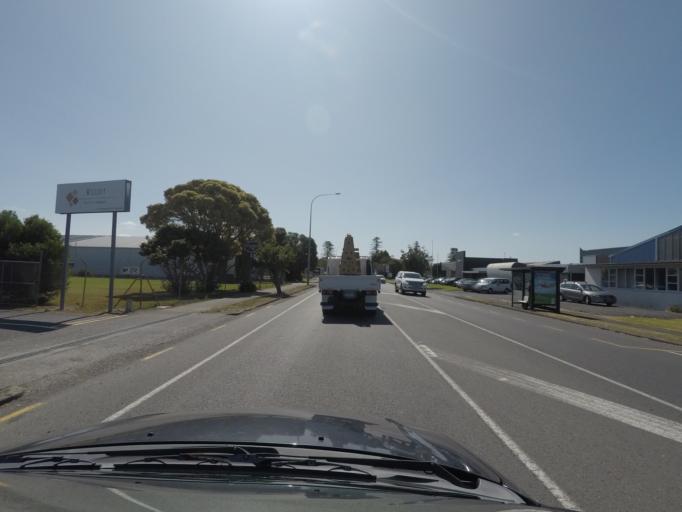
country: NZ
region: Auckland
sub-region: Auckland
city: Rosebank
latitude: -36.8818
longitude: 174.6772
